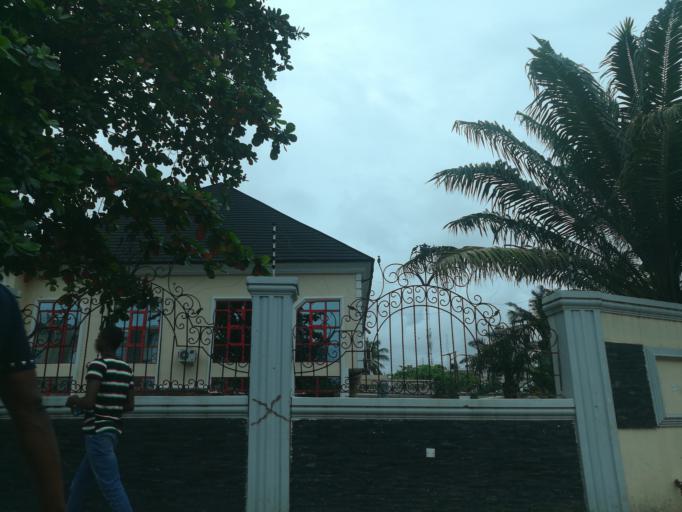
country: NG
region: Lagos
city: Ikoyi
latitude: 6.4315
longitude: 3.4196
